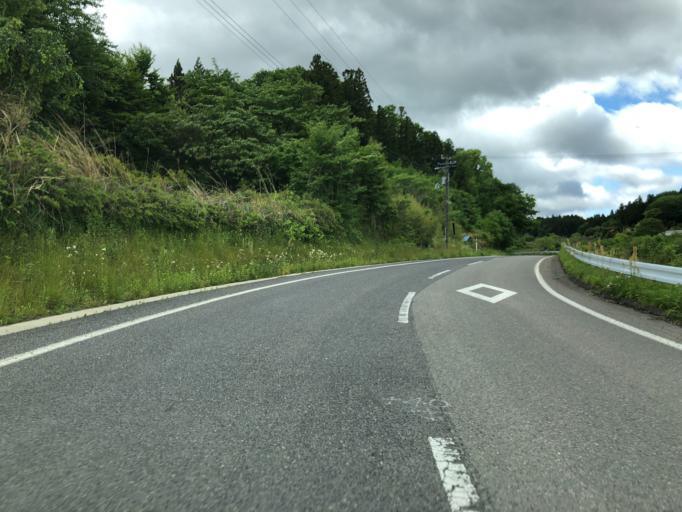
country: JP
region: Fukushima
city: Motomiya
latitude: 37.5160
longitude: 140.4742
